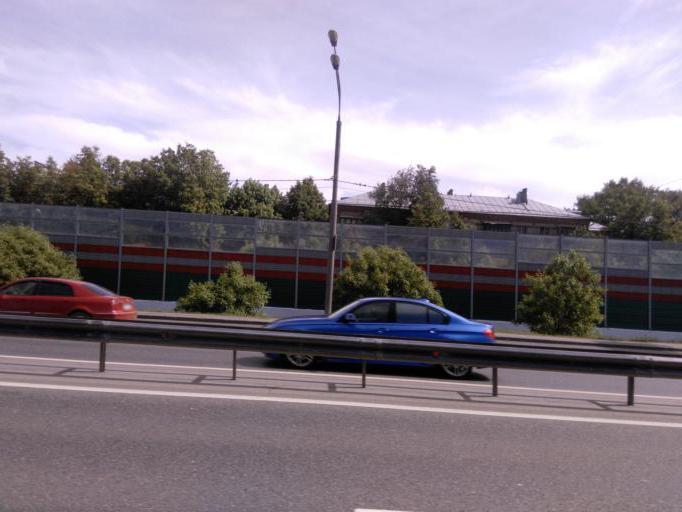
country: RU
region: Moscow
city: Khimki
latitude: 55.8895
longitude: 37.4349
